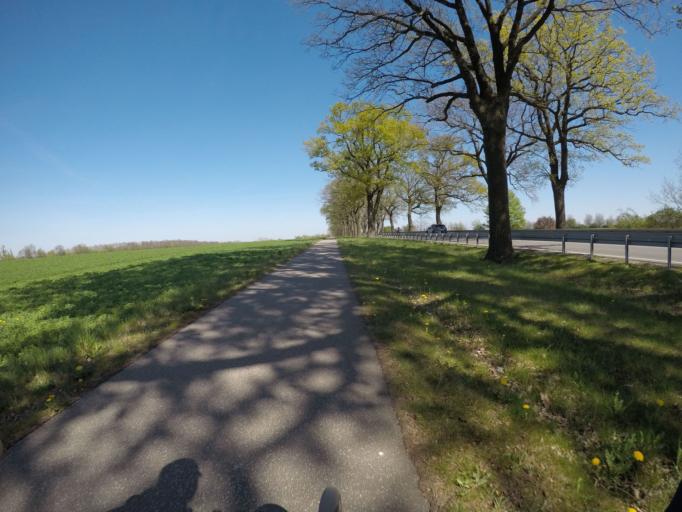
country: DE
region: Brandenburg
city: Werneuchen
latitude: 52.6283
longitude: 13.7144
